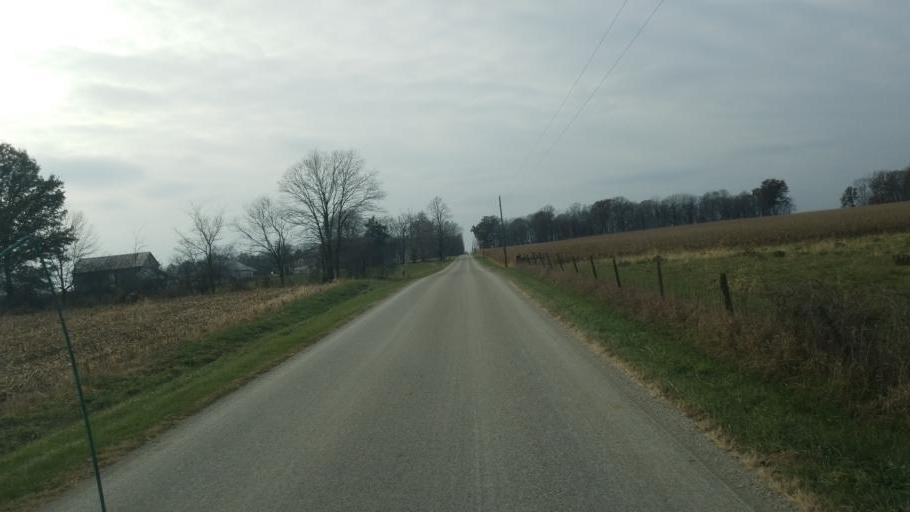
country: US
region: Indiana
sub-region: Adams County
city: Geneva
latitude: 40.6062
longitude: -84.9774
